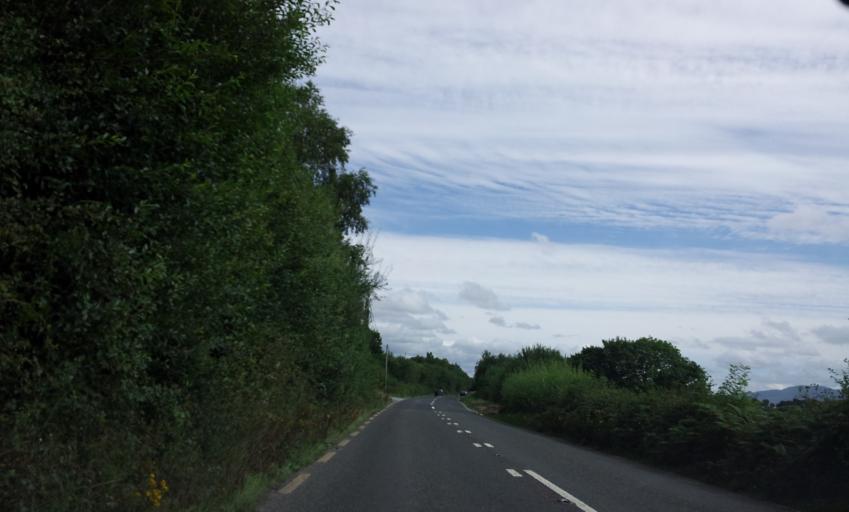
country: IE
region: Munster
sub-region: Ciarrai
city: Killorglin
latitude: 52.0758
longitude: -9.6521
